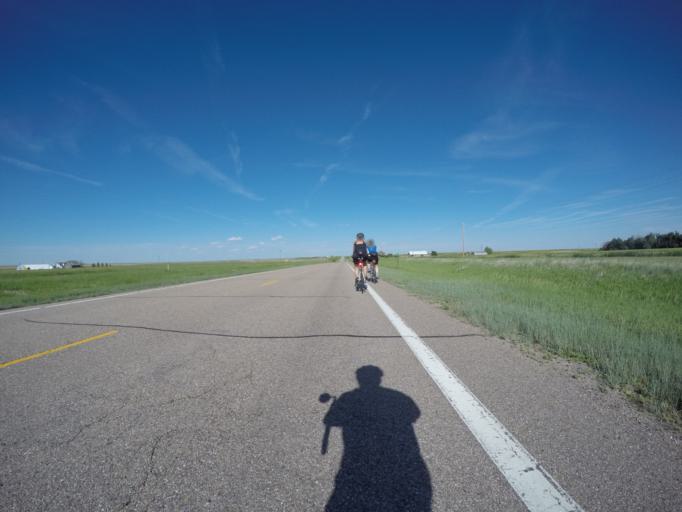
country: US
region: Kansas
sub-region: Cheyenne County
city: Saint Francis
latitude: 39.7565
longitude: -102.0337
